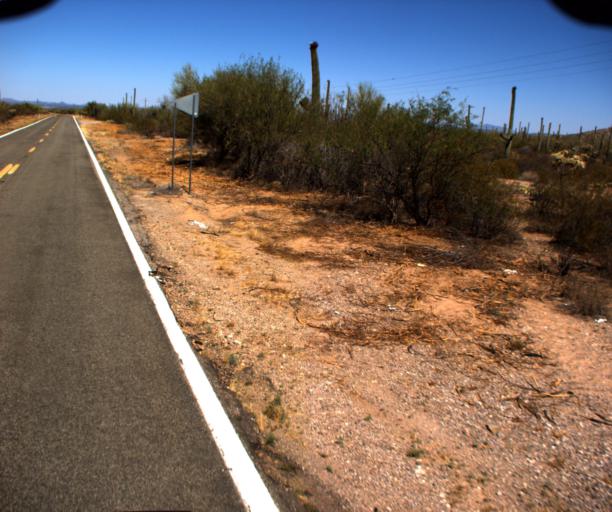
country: US
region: Arizona
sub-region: Pima County
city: Sells
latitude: 32.1767
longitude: -112.2408
